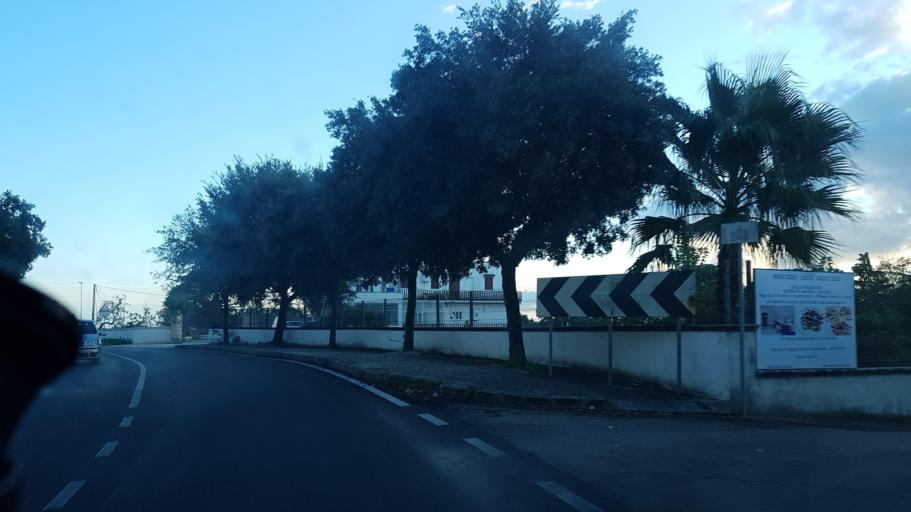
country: IT
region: Apulia
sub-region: Provincia di Brindisi
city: Ostuni
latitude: 40.7192
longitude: 17.5818
